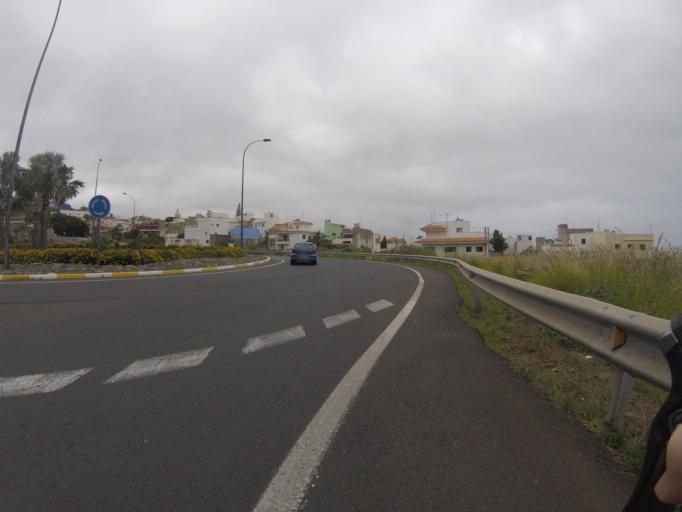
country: ES
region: Canary Islands
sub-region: Provincia de Santa Cruz de Tenerife
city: Tegueste
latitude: 28.5371
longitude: -16.3588
